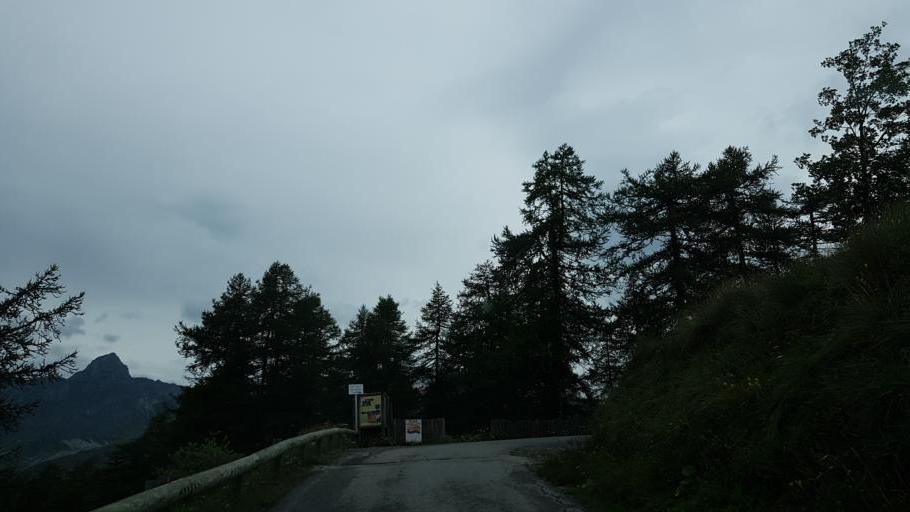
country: IT
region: Piedmont
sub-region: Provincia di Cuneo
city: Serre
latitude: 44.5255
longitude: 7.1025
